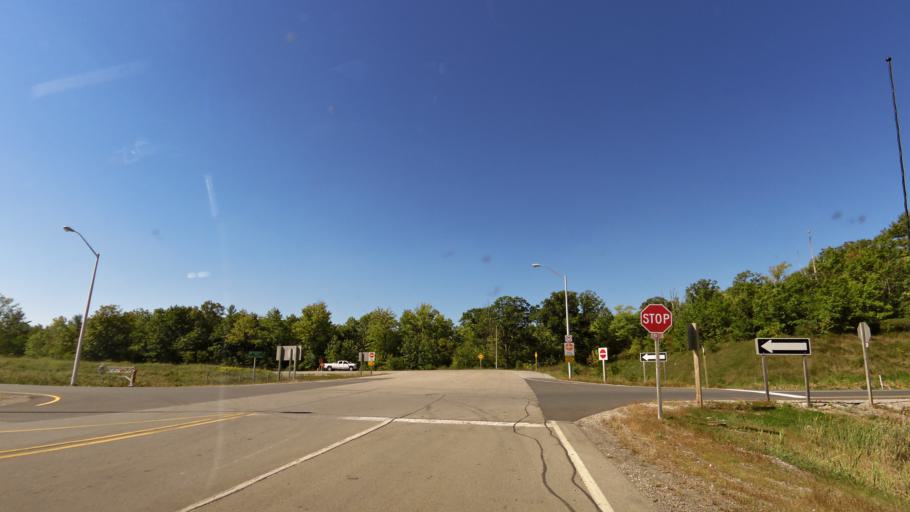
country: CA
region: Ontario
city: Oakville
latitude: 43.4848
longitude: -79.7665
